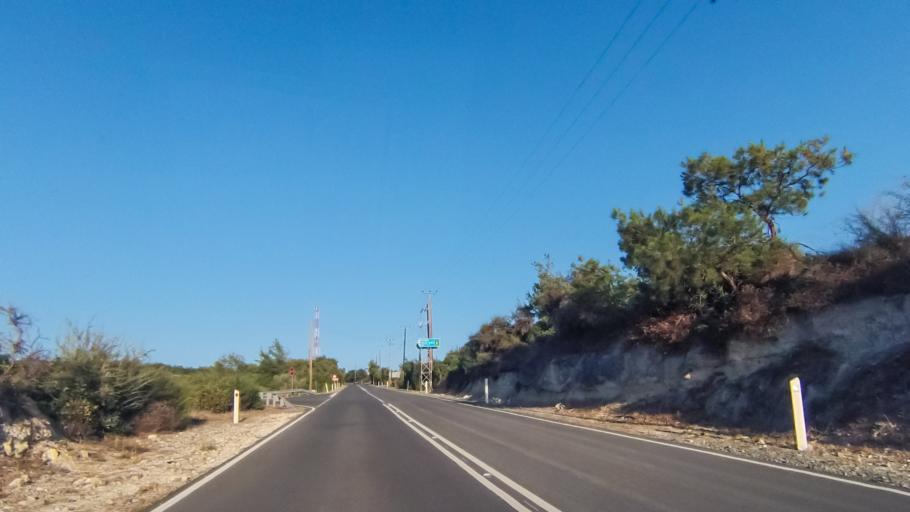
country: CY
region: Limassol
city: Sotira
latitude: 34.6762
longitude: 32.8004
